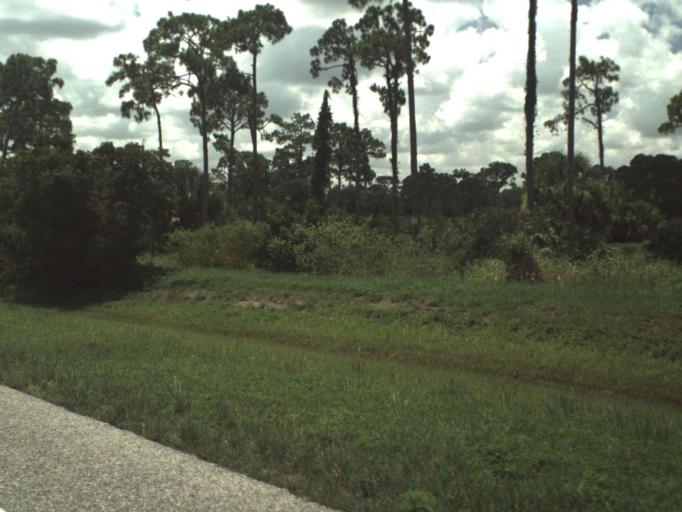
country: US
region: Florida
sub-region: Indian River County
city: Fellsmere
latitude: 27.6748
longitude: -80.8111
